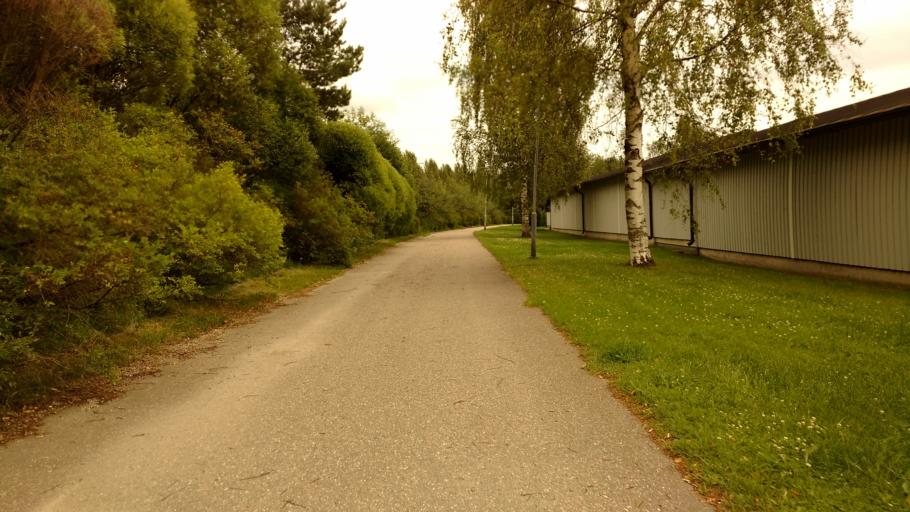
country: FI
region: Varsinais-Suomi
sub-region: Salo
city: Salo
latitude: 60.3940
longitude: 23.1262
